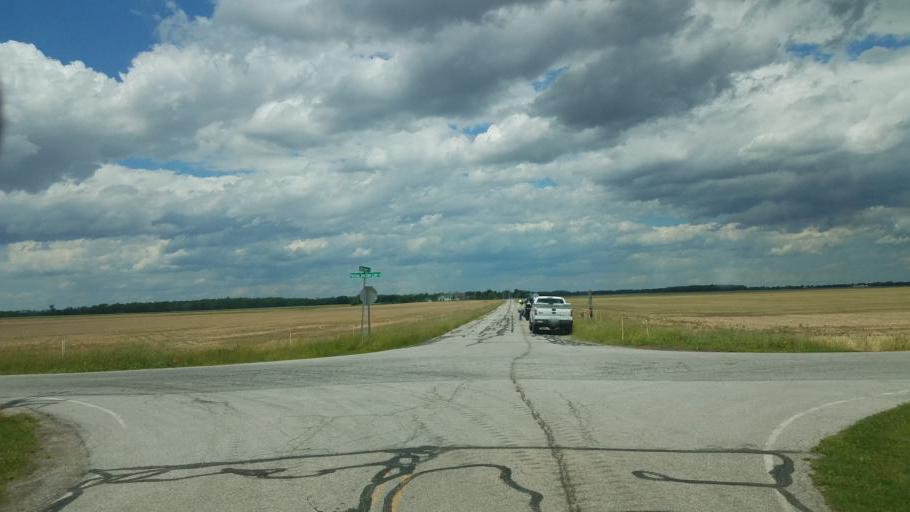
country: US
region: Ohio
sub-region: Huron County
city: Monroeville
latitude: 41.1788
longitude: -82.7673
